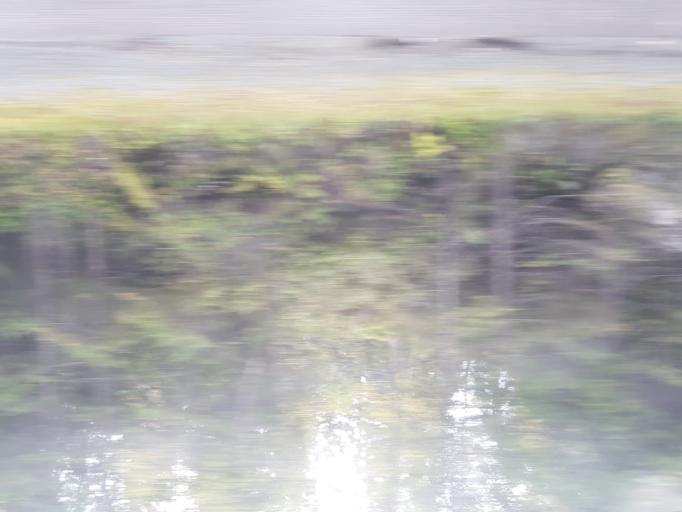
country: NO
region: Sor-Trondelag
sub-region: Trondheim
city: Trondheim
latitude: 63.4165
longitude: 10.3310
